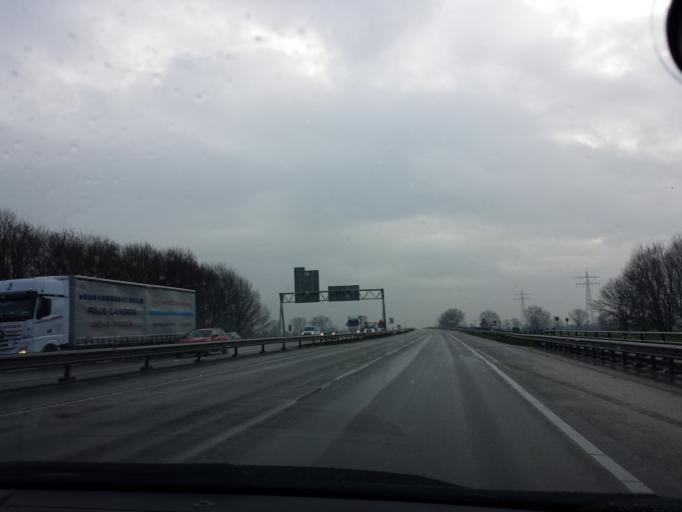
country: NL
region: North Brabant
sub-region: Gemeente Cuijk
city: Cuijk
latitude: 51.7644
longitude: 5.8371
